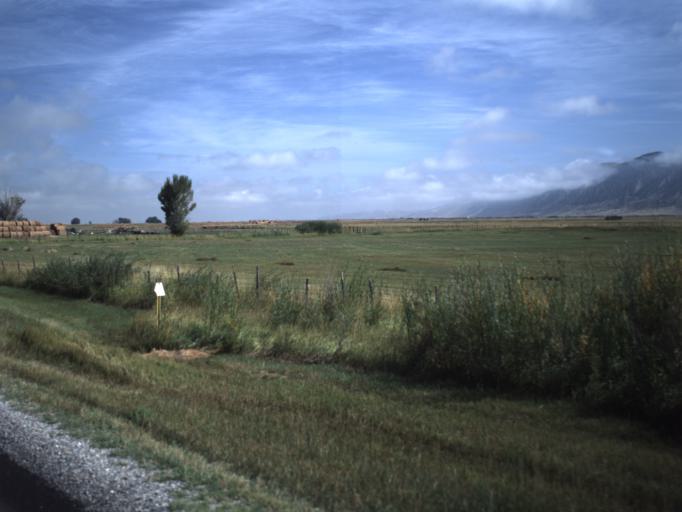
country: US
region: Utah
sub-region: Rich County
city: Randolph
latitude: 41.6200
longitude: -111.1793
